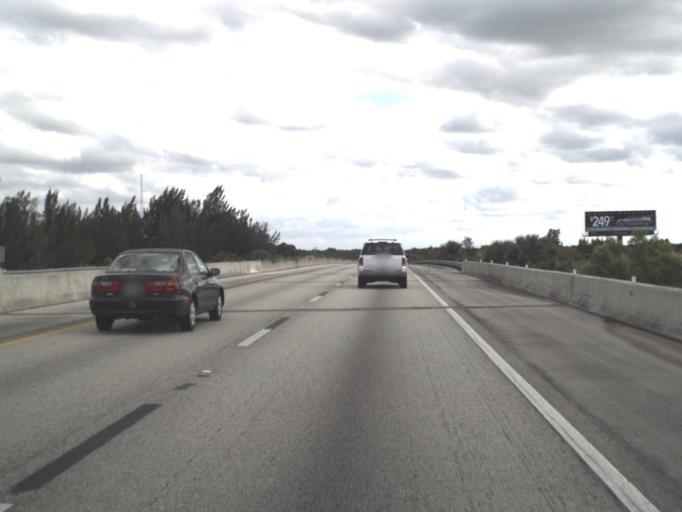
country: US
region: Florida
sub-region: Saint Lucie County
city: Fort Pierce South
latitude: 27.3796
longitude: -80.3866
